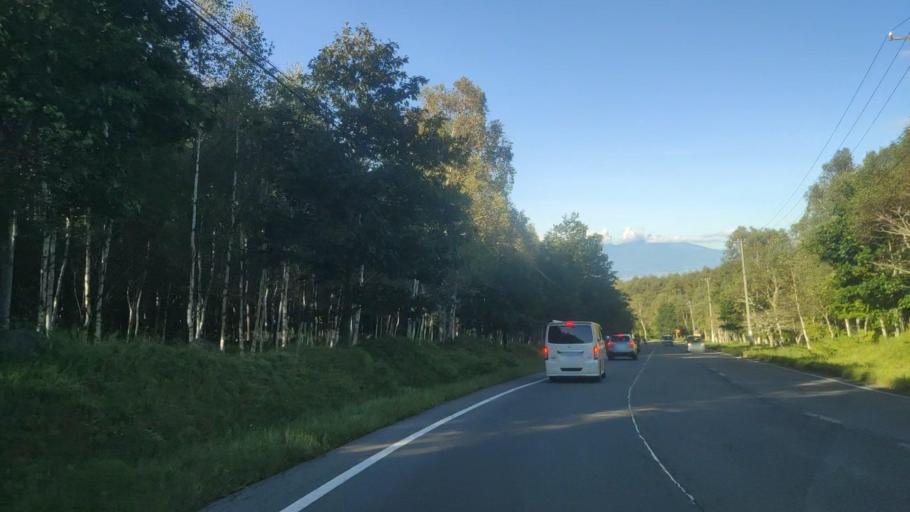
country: JP
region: Nagano
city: Kamimaruko
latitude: 36.1601
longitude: 138.2795
